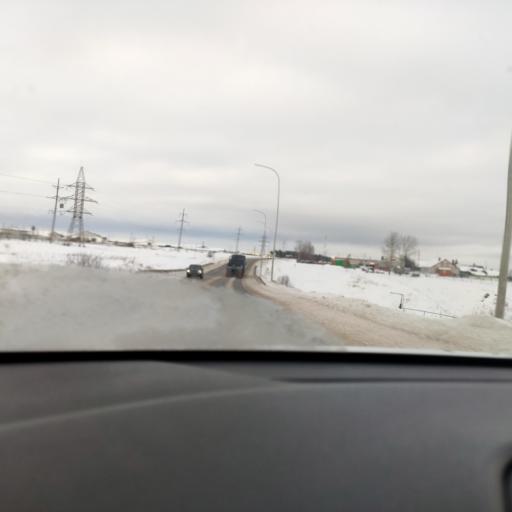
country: RU
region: Tatarstan
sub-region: Arskiy Rayon
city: Arsk
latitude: 56.1979
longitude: 49.9565
